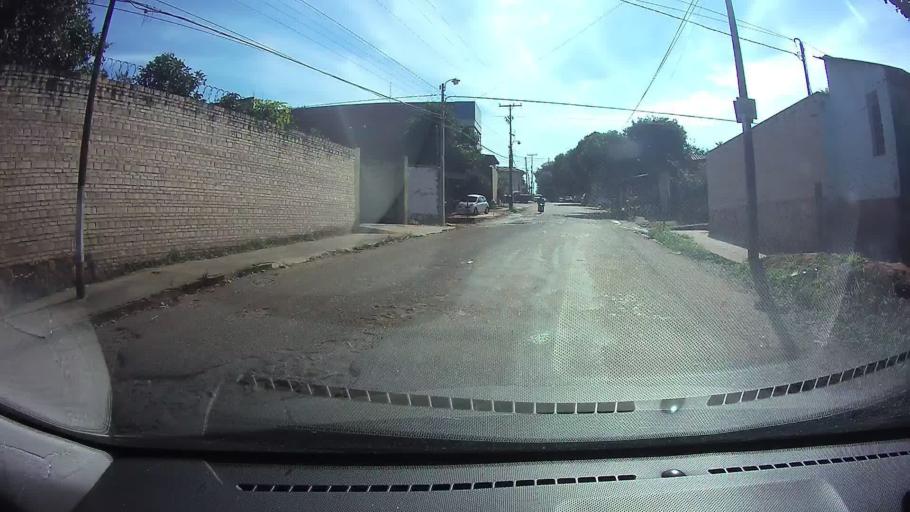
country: PY
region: Central
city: Villa Elisa
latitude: -25.3593
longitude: -57.5697
